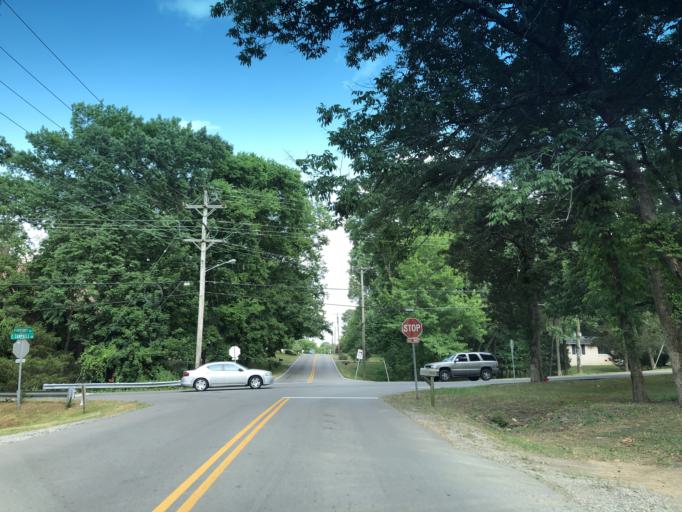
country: US
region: Tennessee
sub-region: Davidson County
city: Goodlettsville
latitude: 36.2767
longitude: -86.7300
